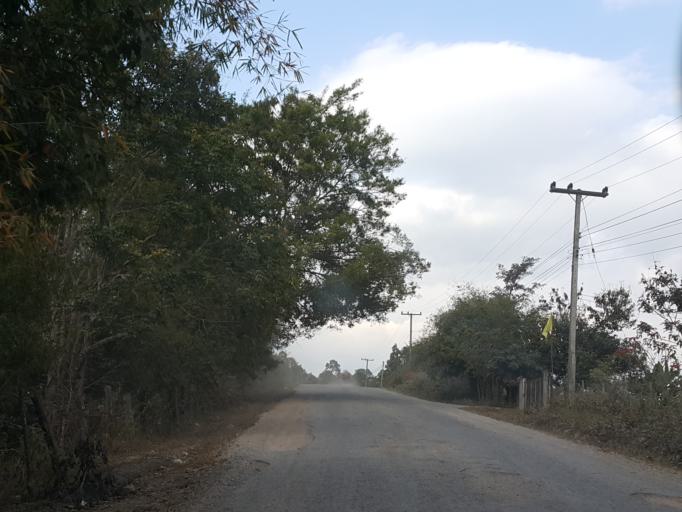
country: TH
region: Chiang Mai
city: Om Koi
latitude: 17.8052
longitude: 98.3320
